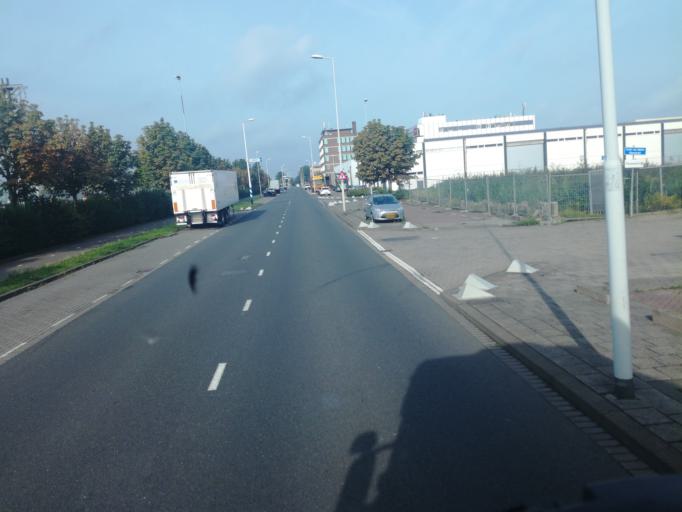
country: NL
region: South Holland
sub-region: Gemeente Albrandswaard
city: Rhoon
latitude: 51.8721
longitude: 4.4431
